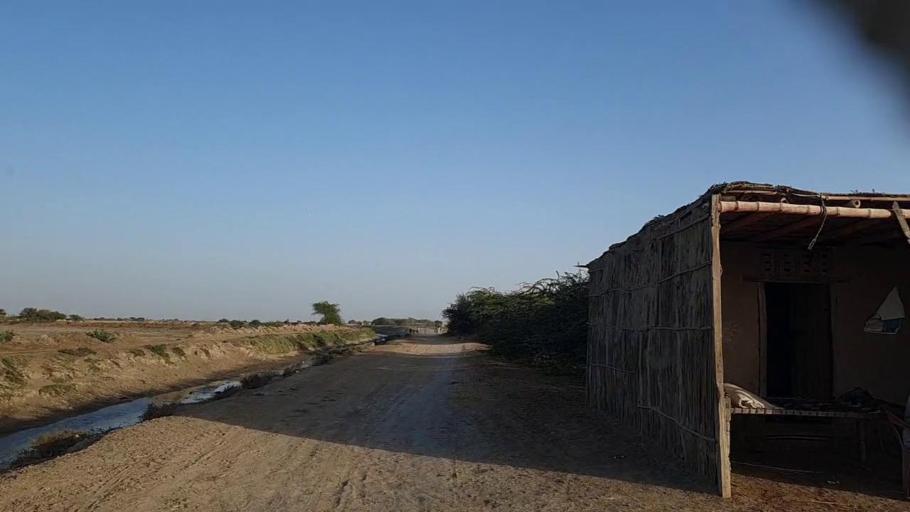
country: PK
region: Sindh
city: Jati
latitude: 24.4052
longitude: 68.3550
